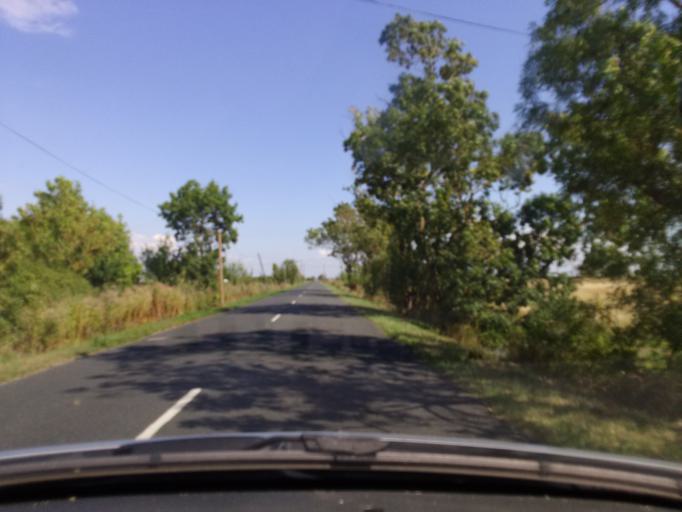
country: FR
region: Pays de la Loire
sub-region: Departement de la Vendee
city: Triaize
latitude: 46.3996
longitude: -1.2328
